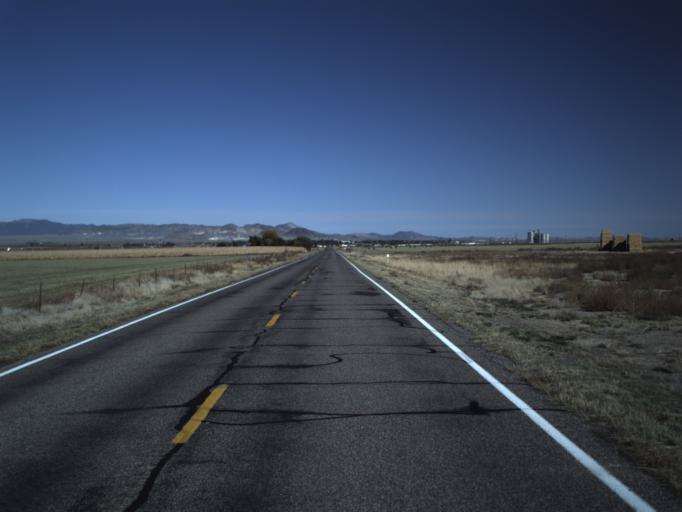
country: US
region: Utah
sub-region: Beaver County
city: Milford
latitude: 38.3560
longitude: -112.9876
